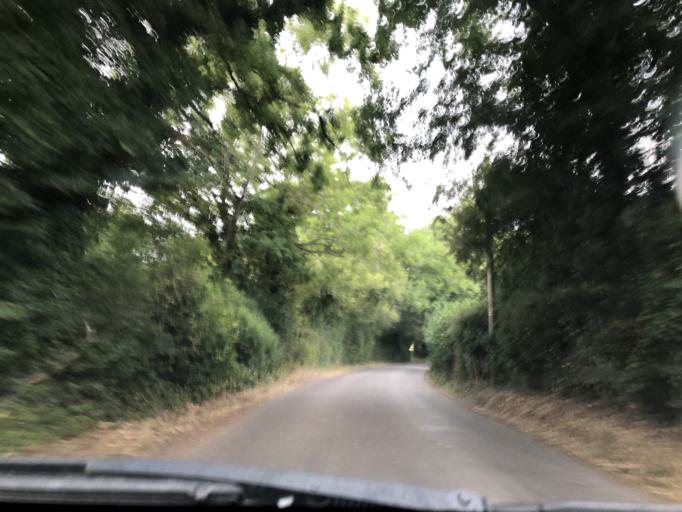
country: GB
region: England
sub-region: Kent
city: Sevenoaks
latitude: 51.2363
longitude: 0.2383
